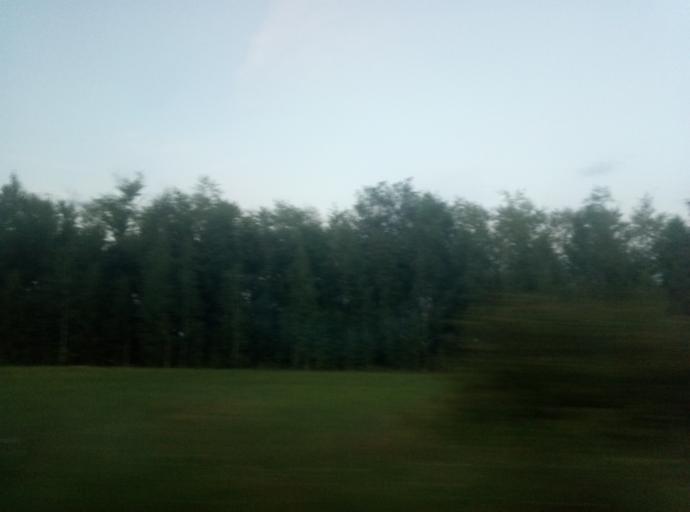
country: RU
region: Tula
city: Kireyevsk
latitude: 53.8554
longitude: 37.8789
